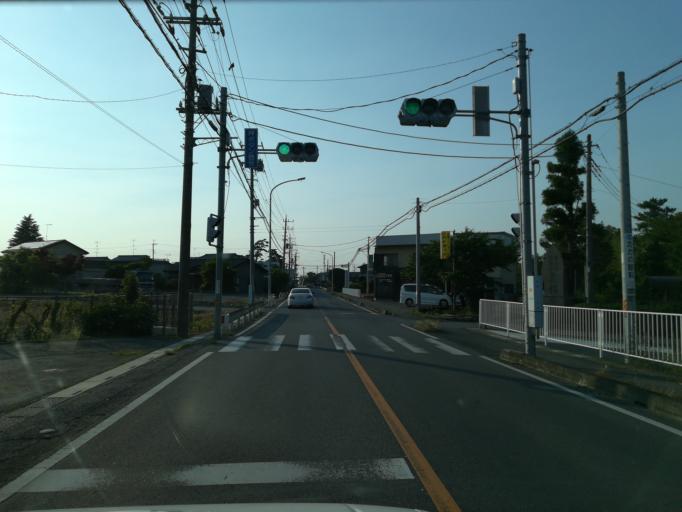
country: JP
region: Saitama
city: Menuma
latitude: 36.1843
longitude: 139.3813
